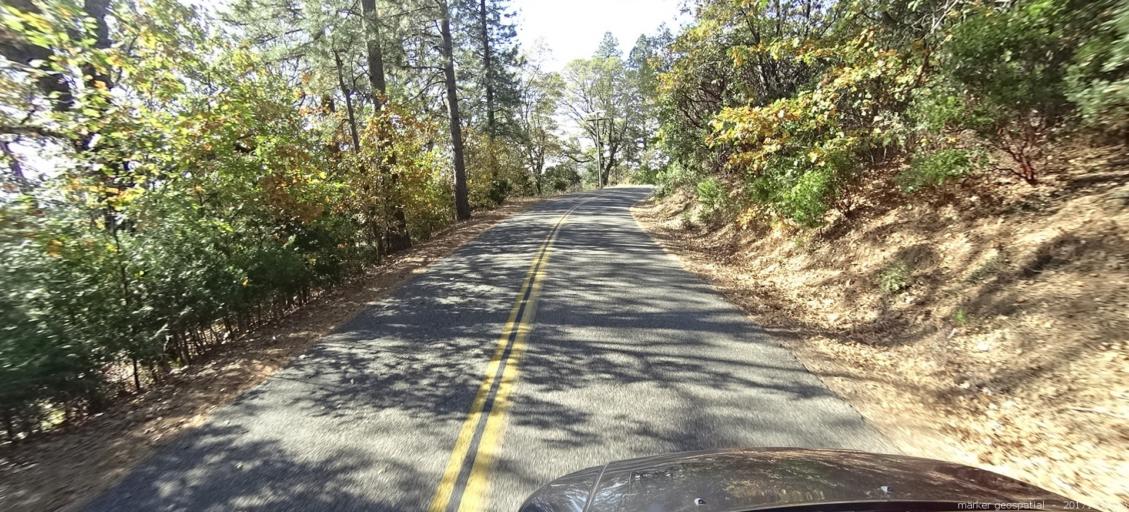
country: US
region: California
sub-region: Shasta County
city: Shingletown
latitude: 40.6874
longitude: -121.9321
